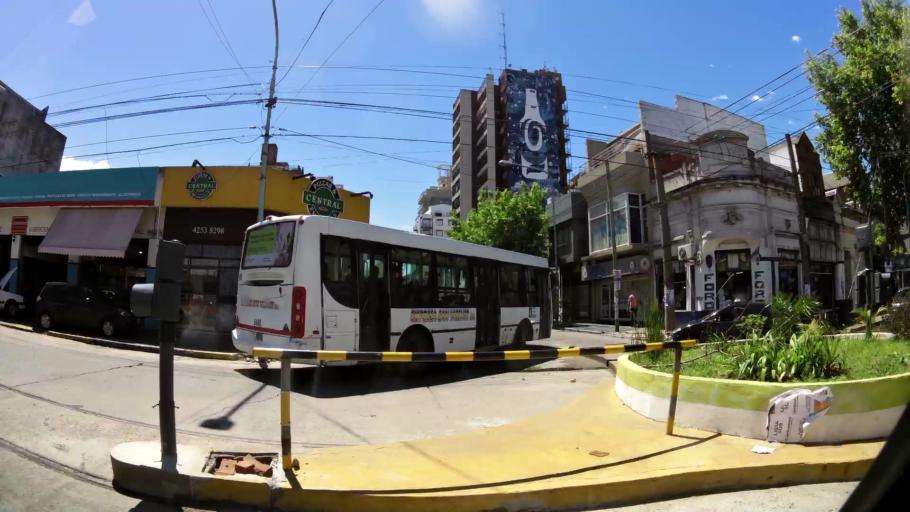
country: AR
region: Buenos Aires
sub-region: Partido de Quilmes
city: Quilmes
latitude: -34.7266
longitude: -58.2579
